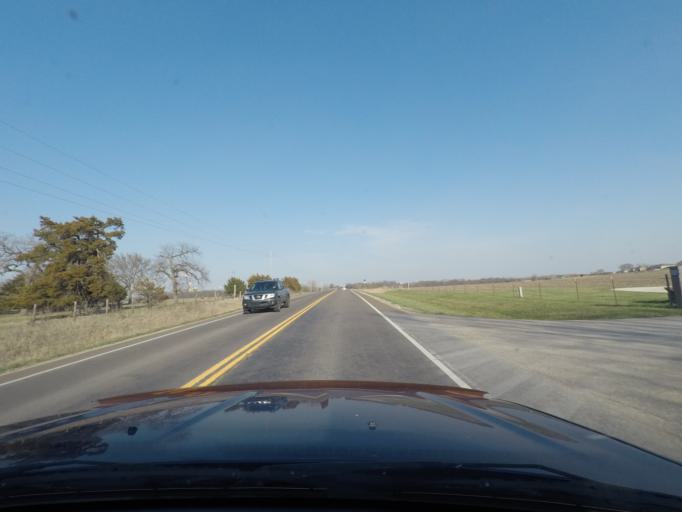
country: US
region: Kansas
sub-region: Douglas County
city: Lawrence
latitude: 39.0006
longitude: -95.2924
